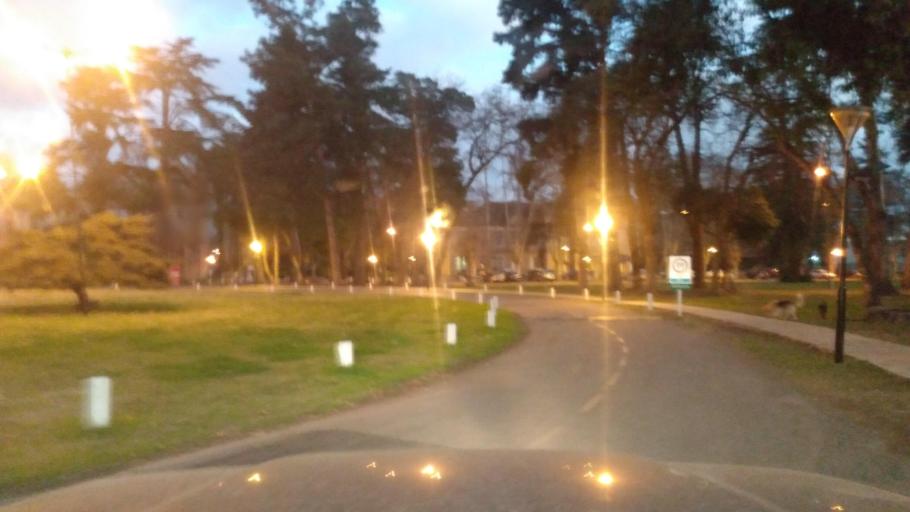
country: AR
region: Buenos Aires
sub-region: Partido de Pilar
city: Pilar
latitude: -34.4375
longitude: -58.8925
